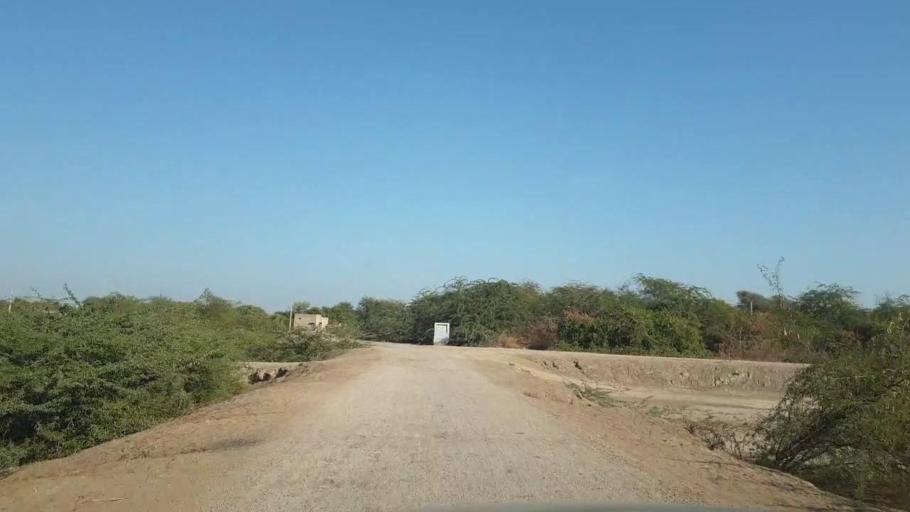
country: PK
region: Sindh
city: Tando Adam
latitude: 25.6868
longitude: 68.6787
